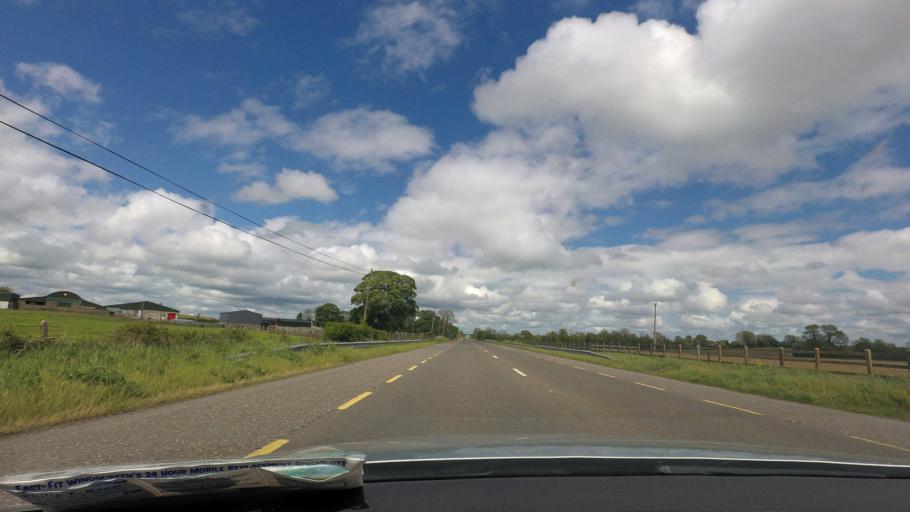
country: IE
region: Munster
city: Thurles
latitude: 52.6046
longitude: -7.7917
